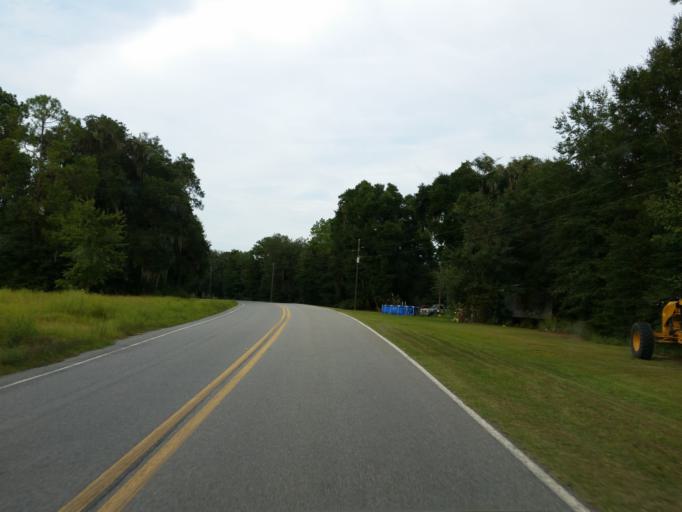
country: US
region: Florida
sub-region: Madison County
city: Madison
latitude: 30.5393
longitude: -83.1924
